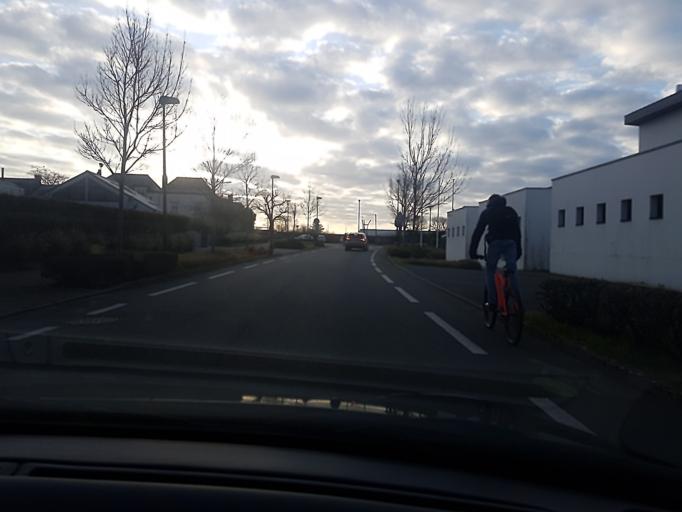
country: FR
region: Pays de la Loire
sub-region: Departement de la Loire-Atlantique
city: Ligne
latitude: 47.4091
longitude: -1.3775
